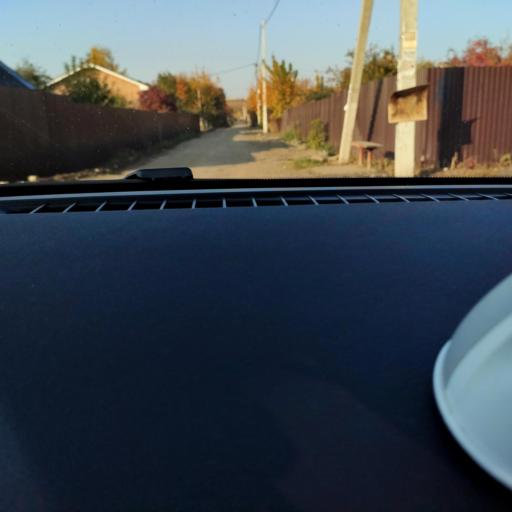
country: RU
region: Samara
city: Petra-Dubrava
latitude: 53.2574
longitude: 50.2717
